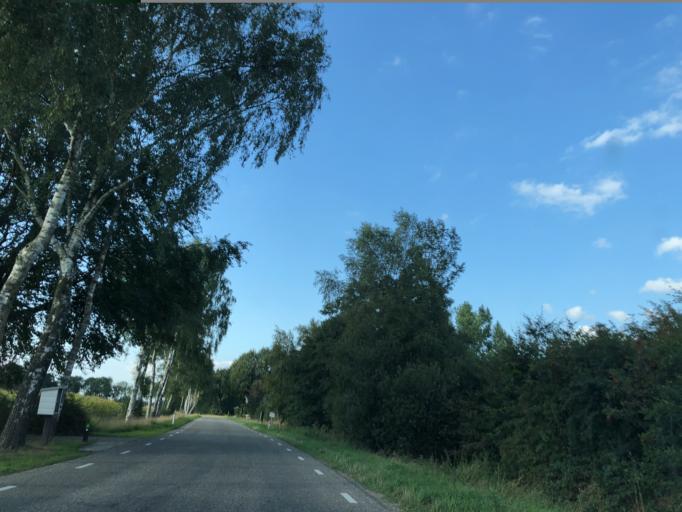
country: NL
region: Groningen
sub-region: Gemeente Vlagtwedde
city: Sellingen
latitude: 53.0026
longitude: 7.2023
